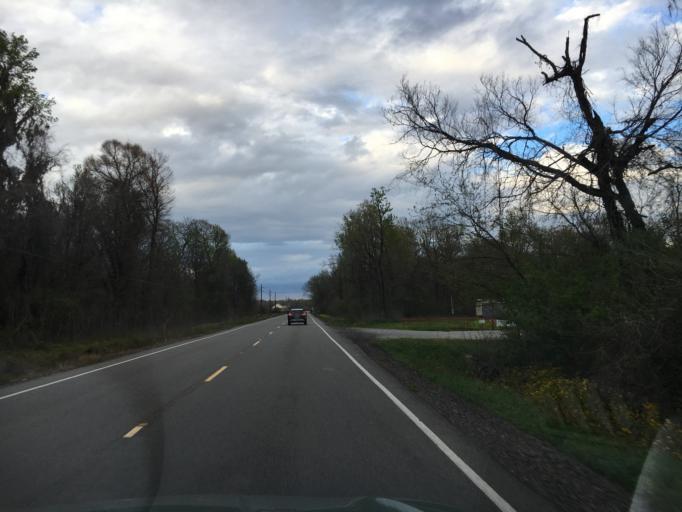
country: US
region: Louisiana
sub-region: West Baton Rouge Parish
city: Erwinville
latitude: 30.4741
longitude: -91.3949
